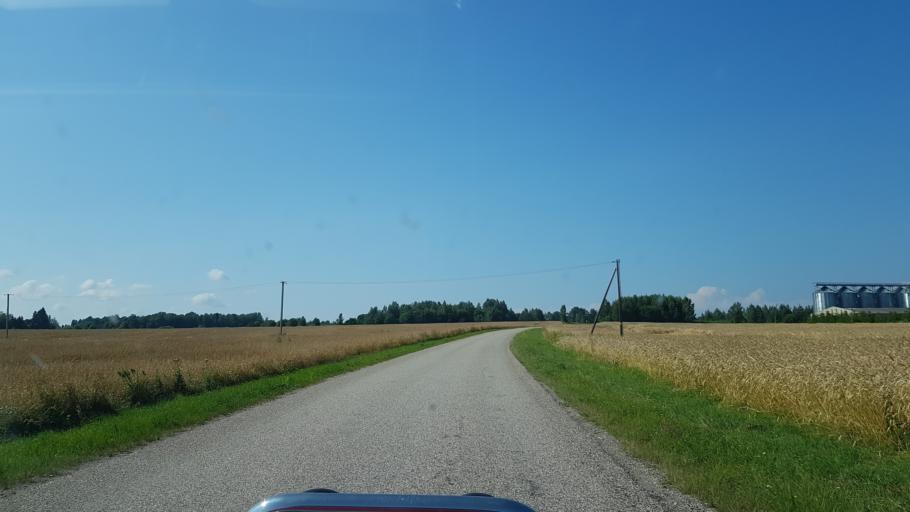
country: EE
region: Tartu
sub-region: Alatskivi vald
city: Kallaste
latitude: 58.5976
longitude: 27.1234
